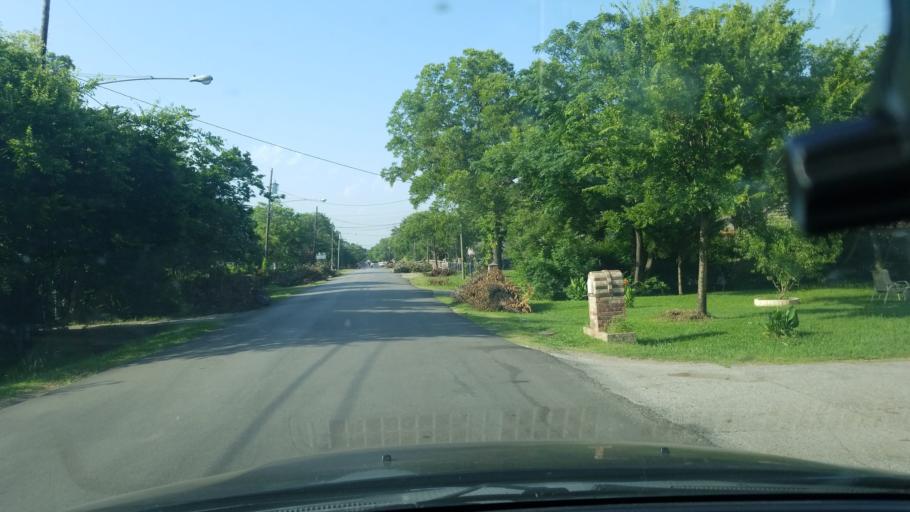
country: US
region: Texas
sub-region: Dallas County
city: Balch Springs
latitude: 32.7283
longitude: -96.6885
